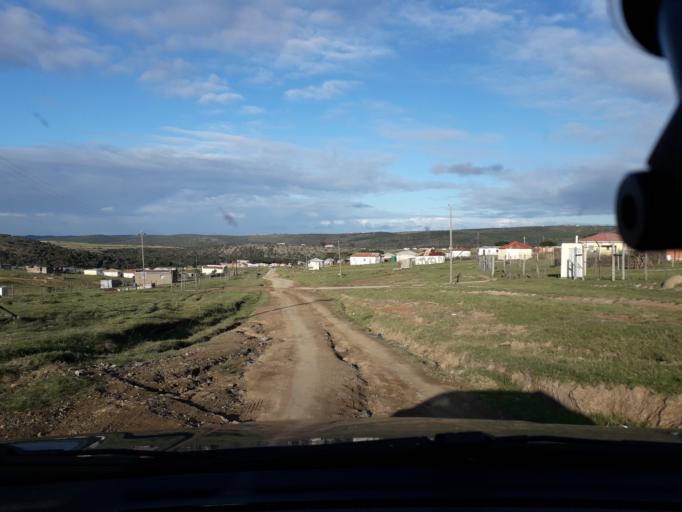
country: ZA
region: Eastern Cape
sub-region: Buffalo City Metropolitan Municipality
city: Bhisho
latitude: -33.1294
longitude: 27.4440
